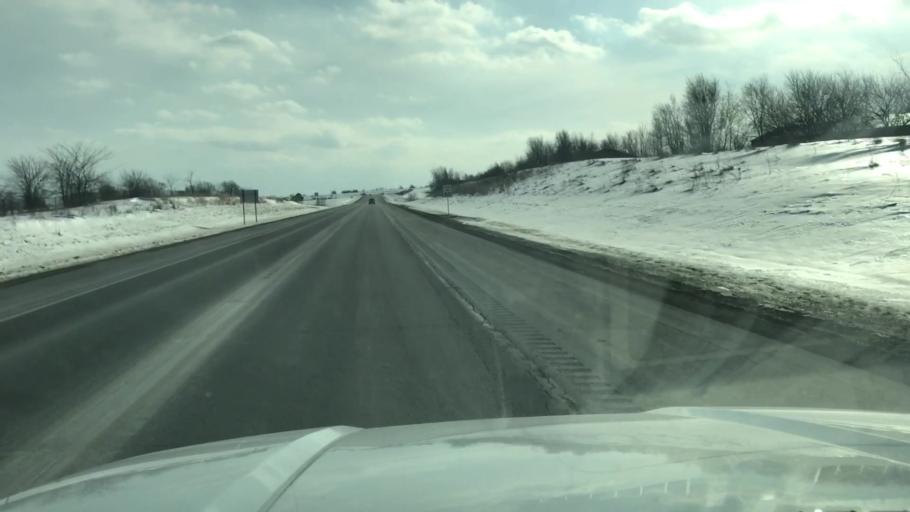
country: US
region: Missouri
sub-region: Nodaway County
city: Maryville
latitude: 40.3425
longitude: -94.8526
